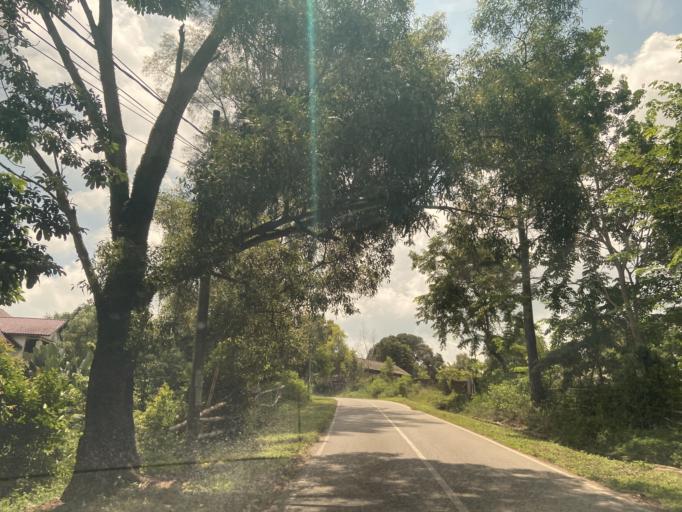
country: SG
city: Singapore
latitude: 1.1546
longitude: 104.0101
